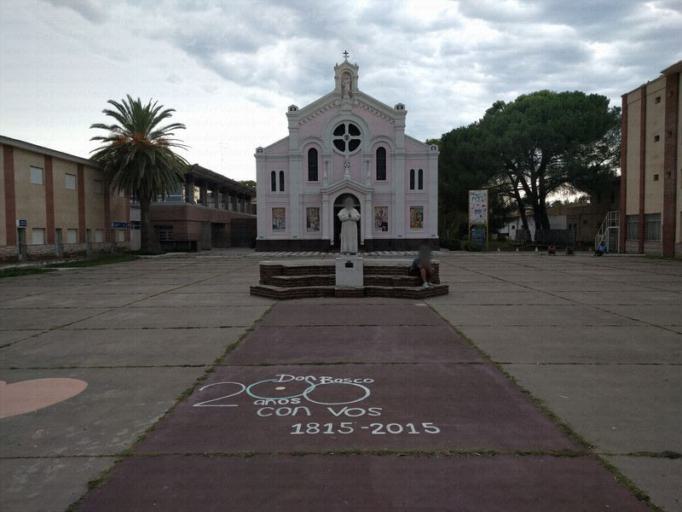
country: AR
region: Buenos Aires
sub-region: Partido de Villarino
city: Medanos
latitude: -39.5241
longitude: -62.6614
